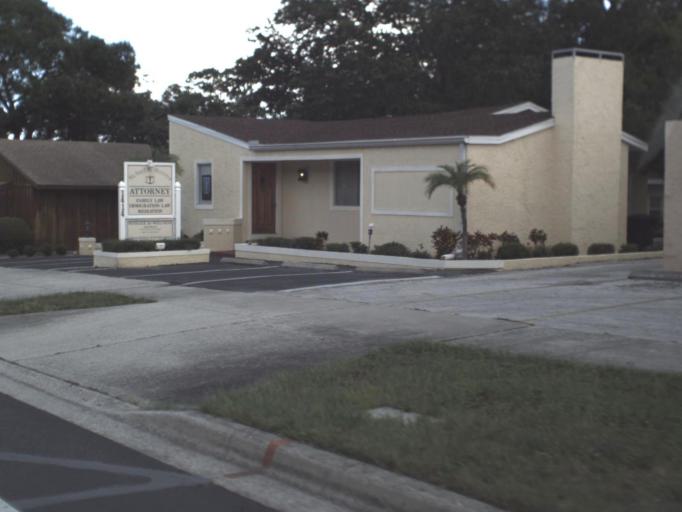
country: US
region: Florida
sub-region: Pinellas County
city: Clearwater
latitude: 27.9608
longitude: -82.7785
